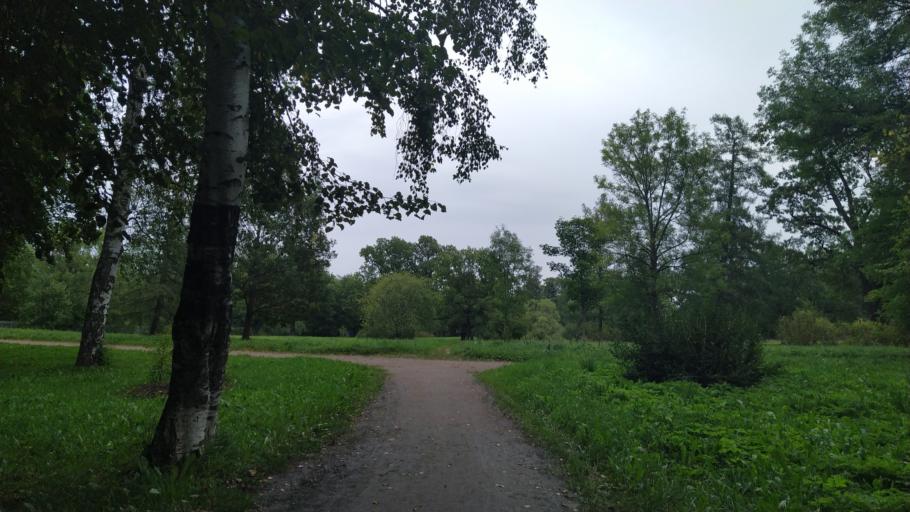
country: RU
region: St.-Petersburg
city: Pushkin
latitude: 59.7228
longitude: 30.3907
